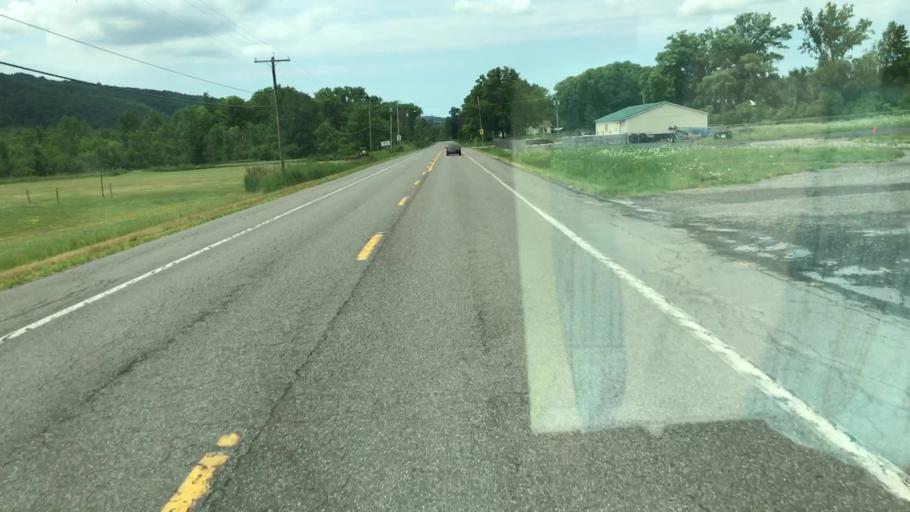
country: US
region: New York
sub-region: Onondaga County
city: Nedrow
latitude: 42.8949
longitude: -76.1545
